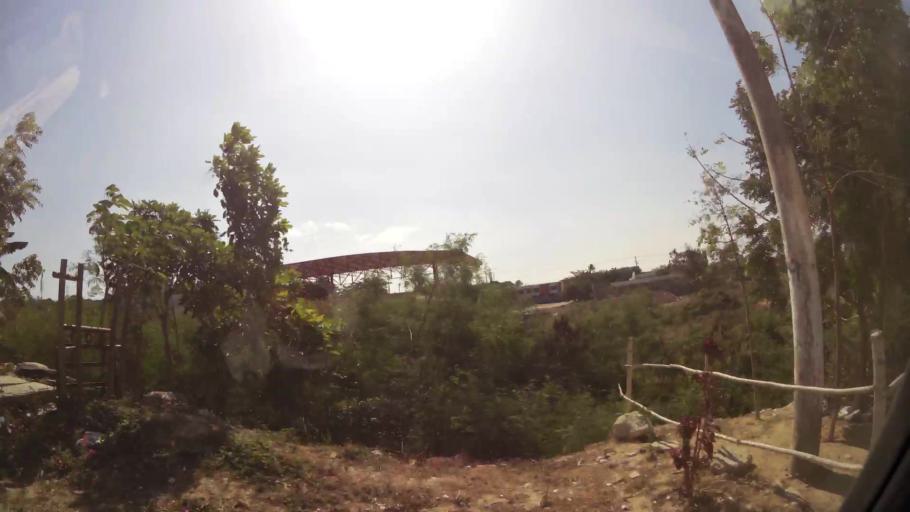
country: CO
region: Atlantico
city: Barranquilla
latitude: 10.9794
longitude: -74.8271
